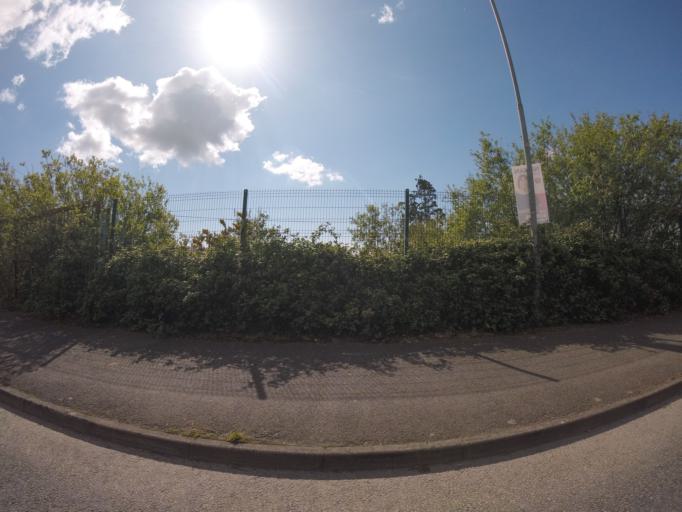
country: IE
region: Munster
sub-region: Waterford
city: Waterford
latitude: 52.2703
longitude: -7.0939
